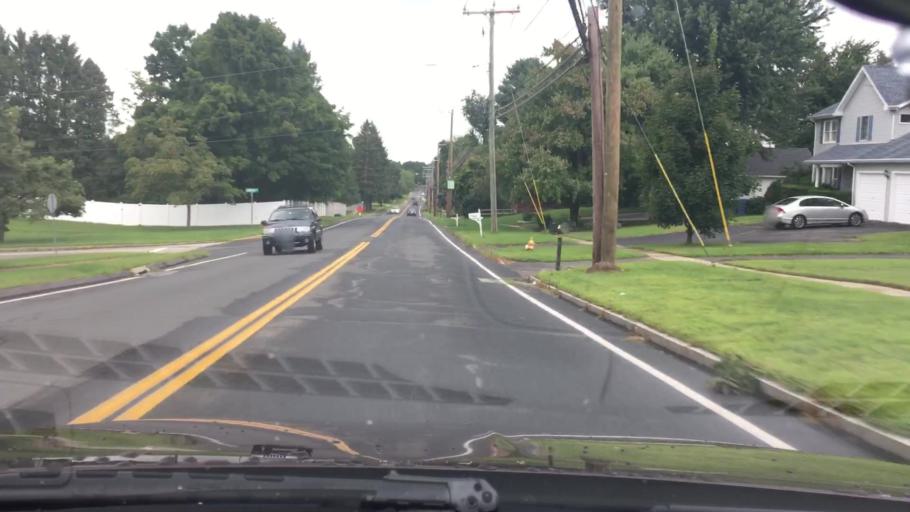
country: US
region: Connecticut
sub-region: Hartford County
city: Manchester
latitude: 41.7520
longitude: -72.5403
